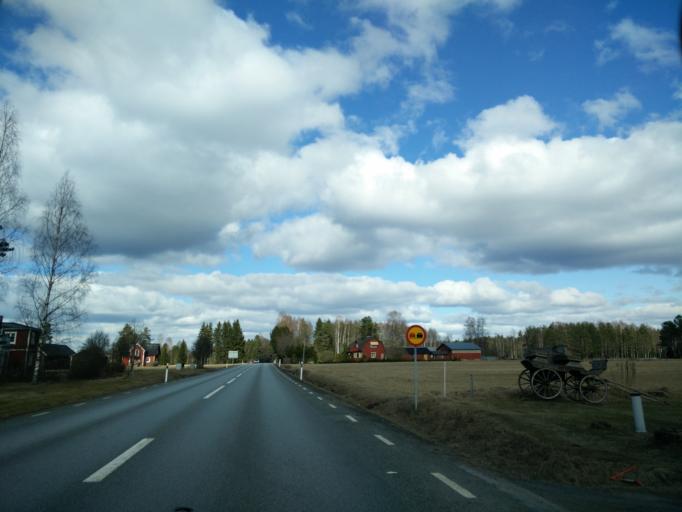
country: SE
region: Vaermland
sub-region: Hagfors Kommun
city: Hagfors
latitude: 59.9696
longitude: 13.5625
